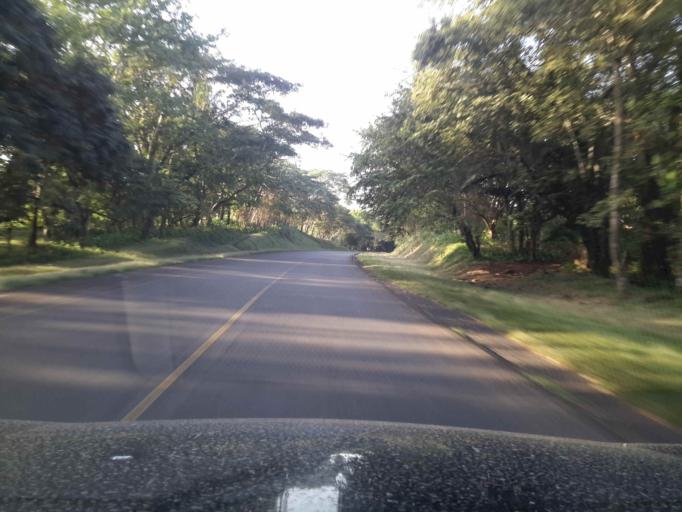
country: NI
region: Rio San Juan
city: San Miguelito
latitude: 11.4269
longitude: -84.8501
